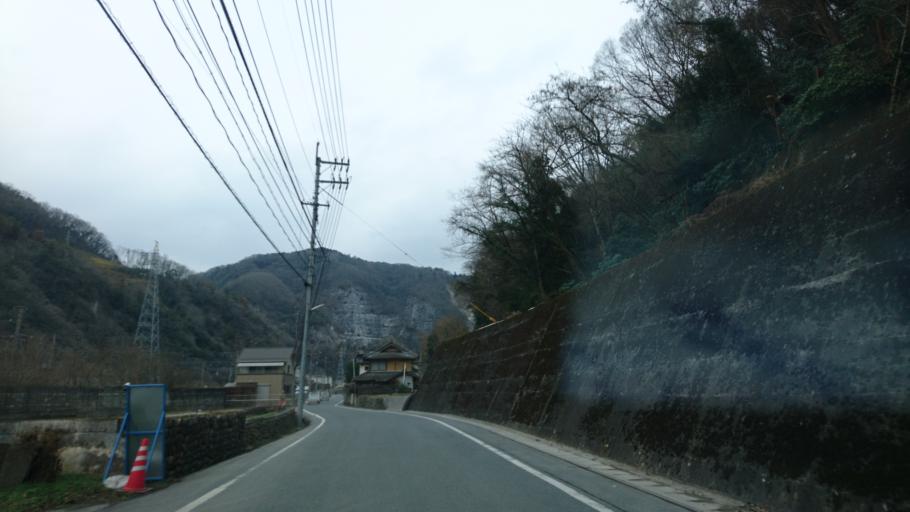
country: JP
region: Okayama
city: Niimi
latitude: 34.9304
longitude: 133.5115
